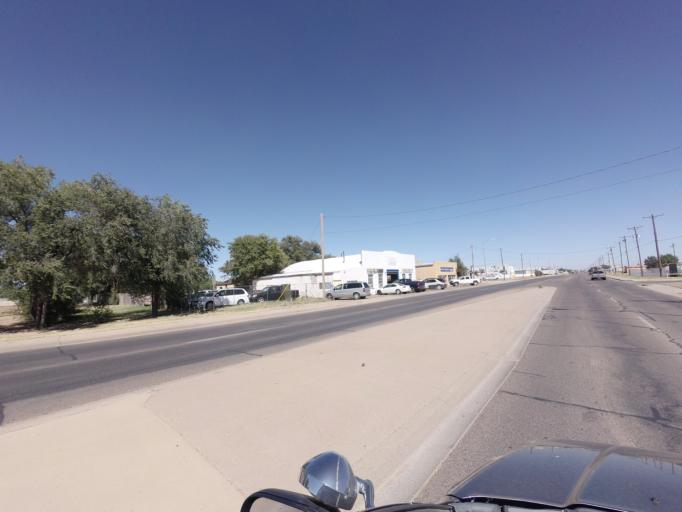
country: US
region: New Mexico
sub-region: Curry County
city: Clovis
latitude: 34.4046
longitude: -103.2311
